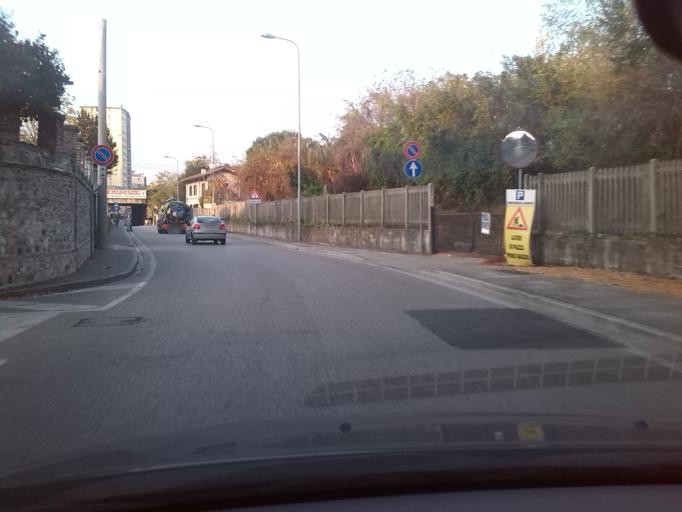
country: IT
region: Friuli Venezia Giulia
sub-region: Provincia di Udine
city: Udine
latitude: 46.0517
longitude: 13.2303
